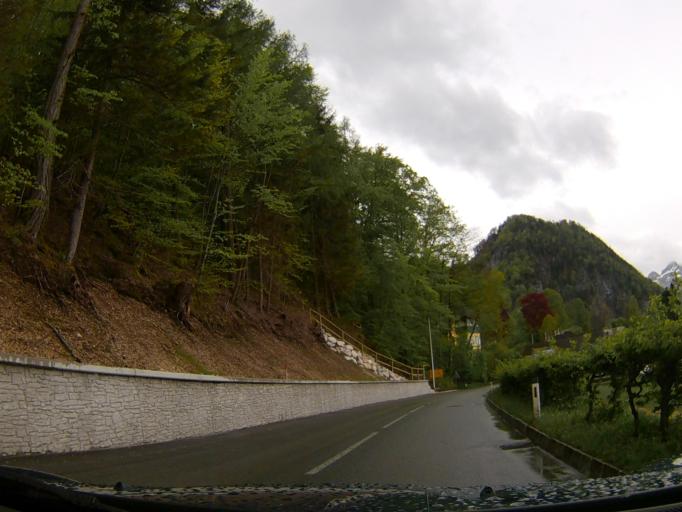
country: AT
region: Upper Austria
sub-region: Politischer Bezirk Vocklabruck
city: Steinbach am Attersee
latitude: 47.8013
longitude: 13.5440
